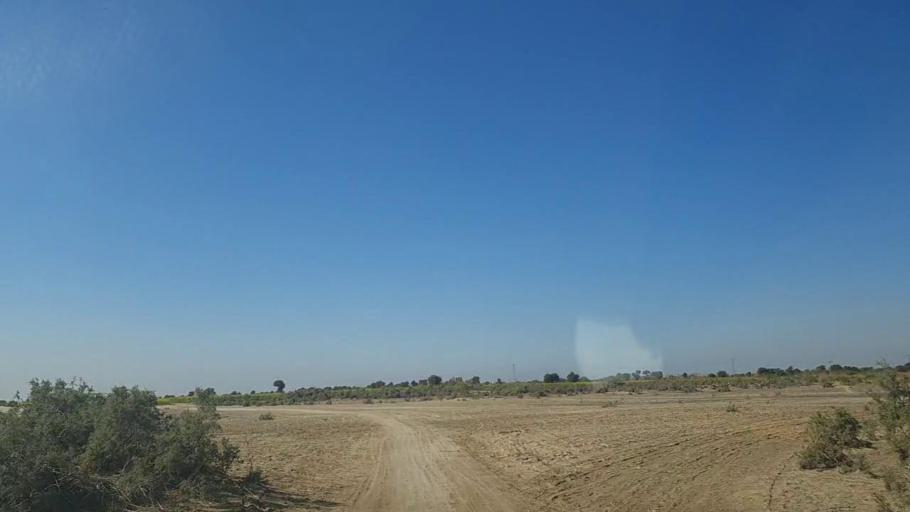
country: PK
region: Sindh
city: Khadro
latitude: 26.1576
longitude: 68.8231
